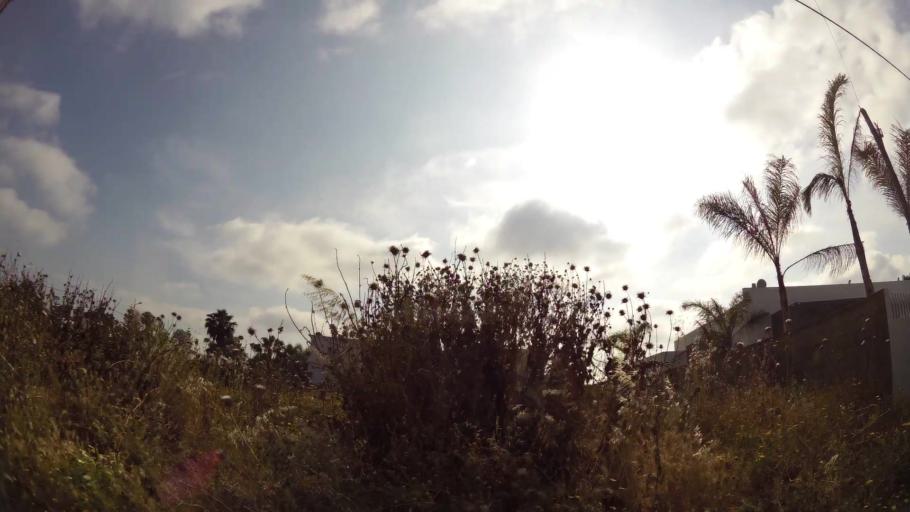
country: MA
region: Rabat-Sale-Zemmour-Zaer
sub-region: Rabat
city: Rabat
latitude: 33.9651
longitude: -6.8422
